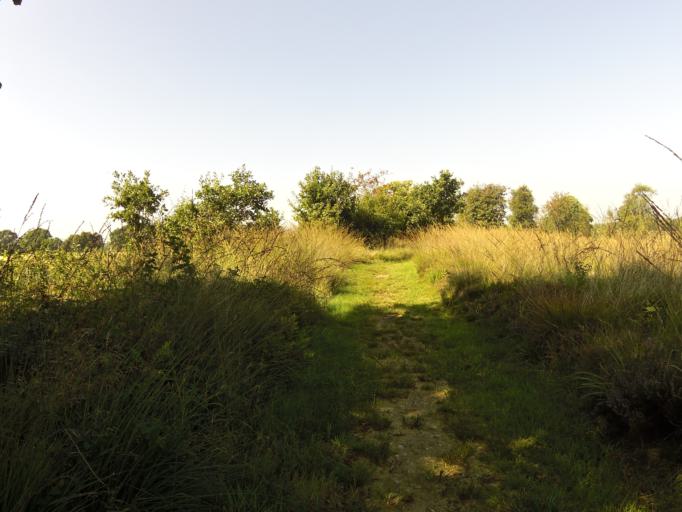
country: DK
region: South Denmark
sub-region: Aabenraa Kommune
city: Krusa
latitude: 54.9354
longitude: 9.4636
